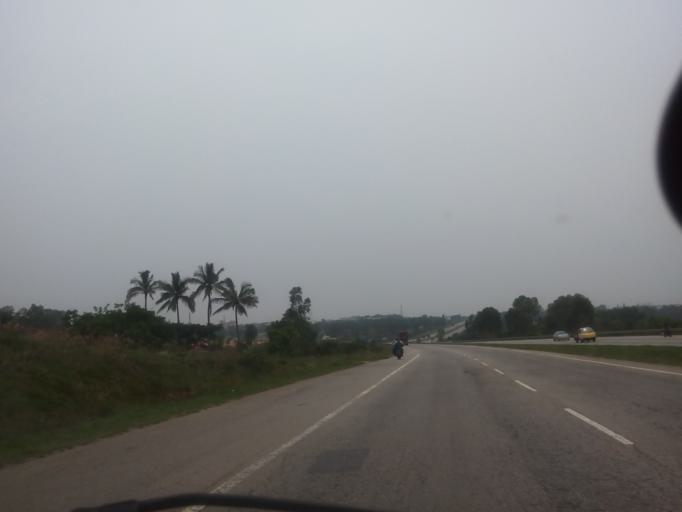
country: IN
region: Karnataka
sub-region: Bangalore Urban
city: Bangalore
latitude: 12.8546
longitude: 77.6084
